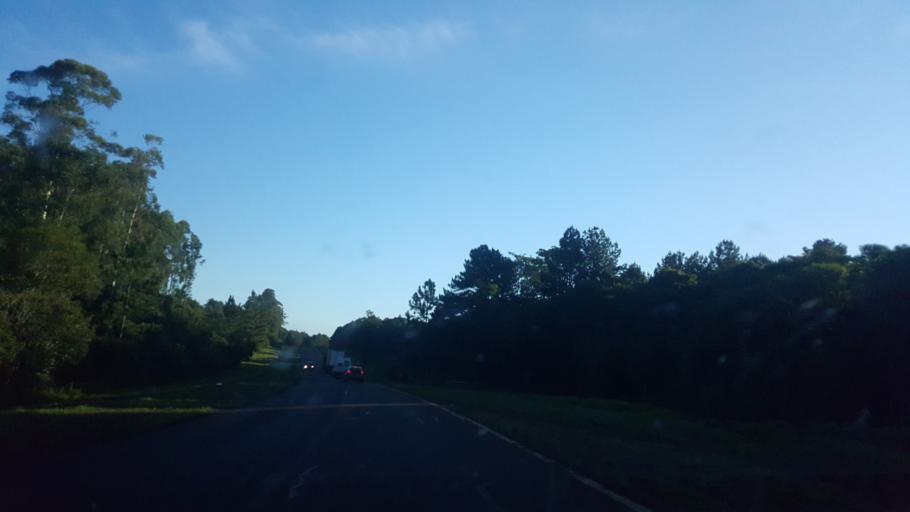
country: AR
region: Misiones
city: El Alcazar
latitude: -26.7334
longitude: -54.8747
